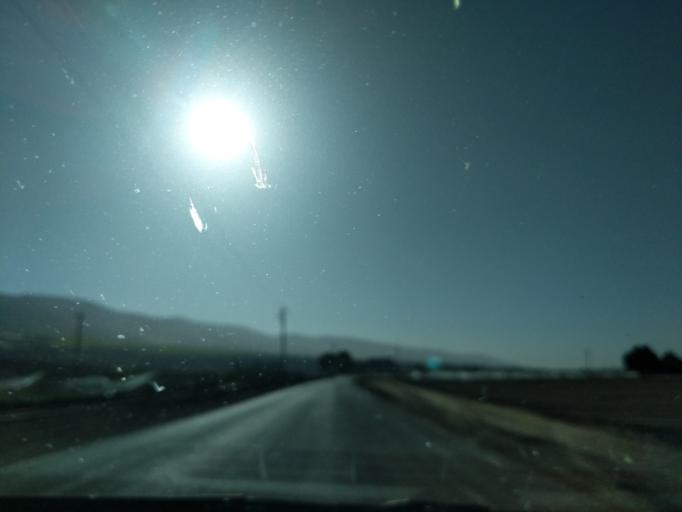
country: US
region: California
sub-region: Monterey County
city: Soledad
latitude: 36.4079
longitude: -121.3718
